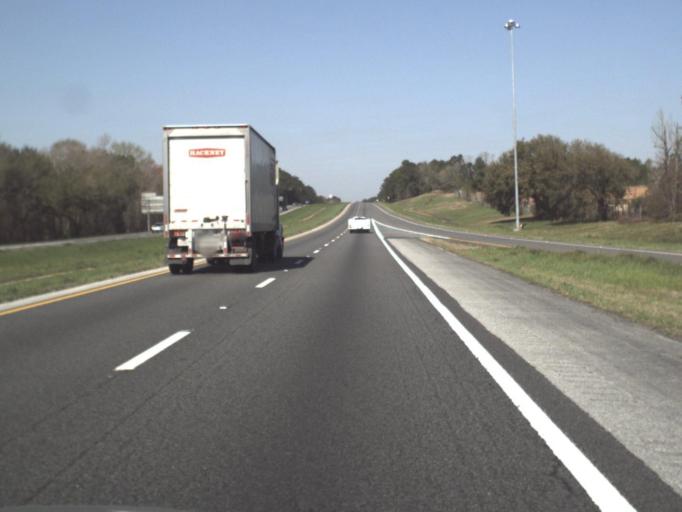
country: US
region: Florida
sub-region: Jackson County
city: Sneads
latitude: 30.6595
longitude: -85.0422
